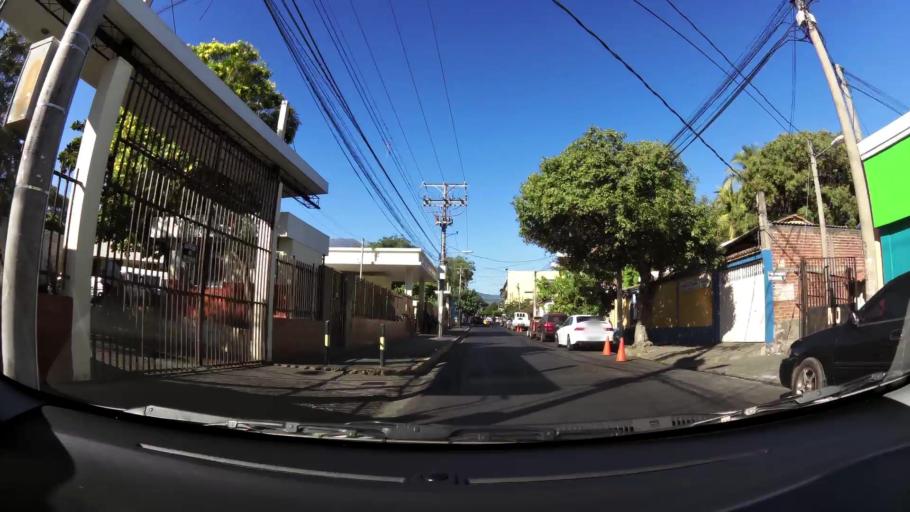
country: SV
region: San Miguel
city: San Miguel
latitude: 13.4764
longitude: -88.1816
